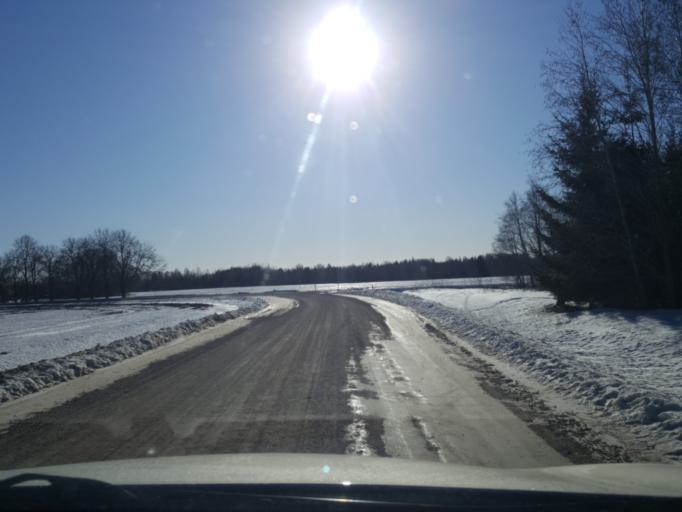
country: EE
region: Viljandimaa
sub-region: Viljandi linn
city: Viljandi
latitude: 58.4621
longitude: 25.5825
